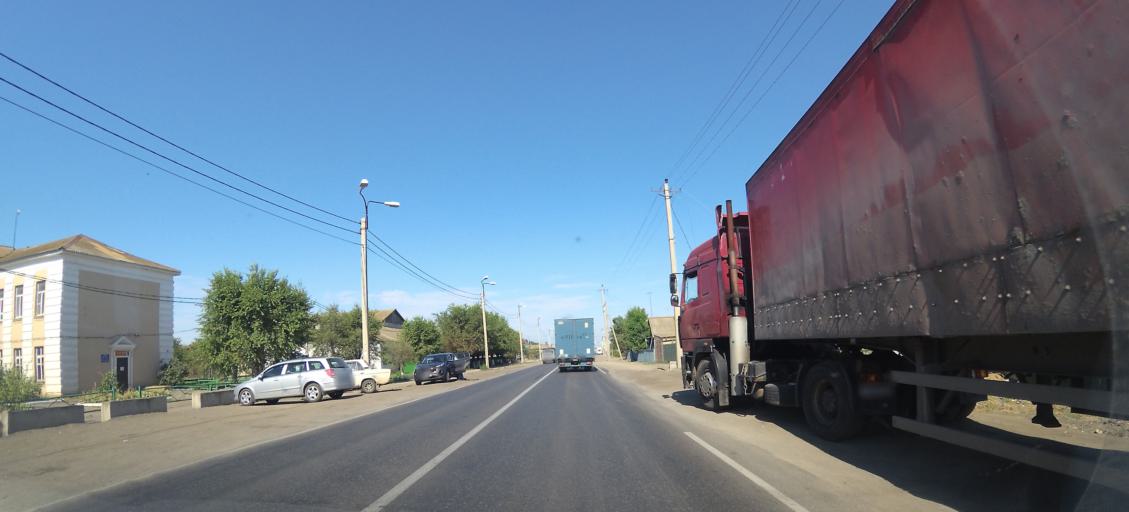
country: RU
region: Volgograd
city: Novyy Rogachik
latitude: 48.6793
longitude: 44.0550
